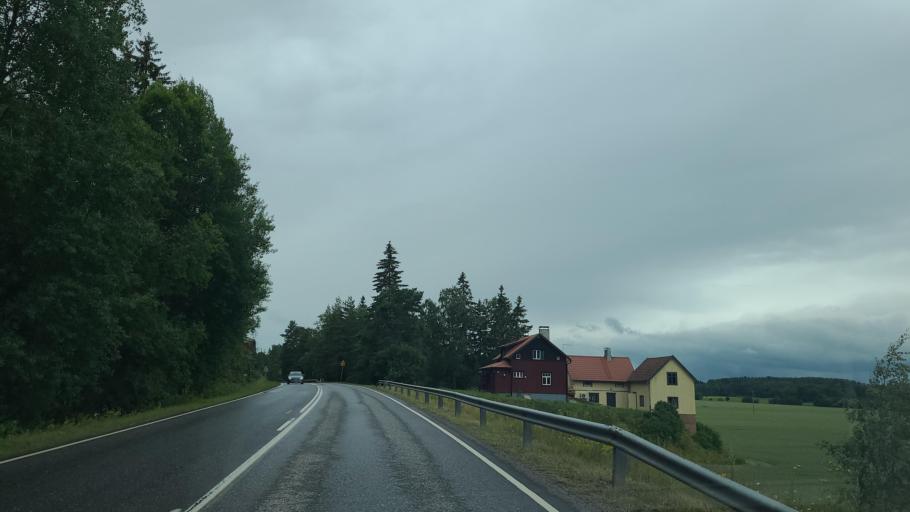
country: FI
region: Varsinais-Suomi
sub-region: Turku
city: Sauvo
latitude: 60.3155
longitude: 22.6954
